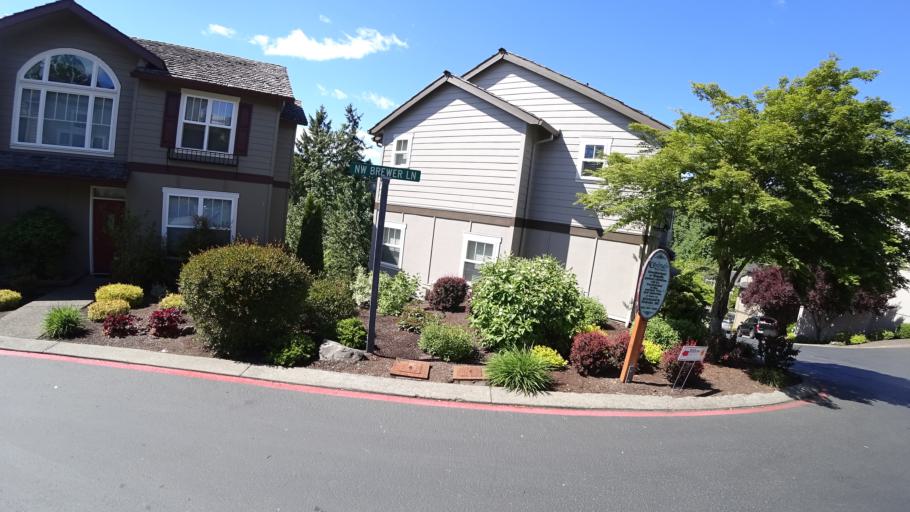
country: US
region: Oregon
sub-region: Washington County
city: West Haven
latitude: 45.5418
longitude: -122.7805
